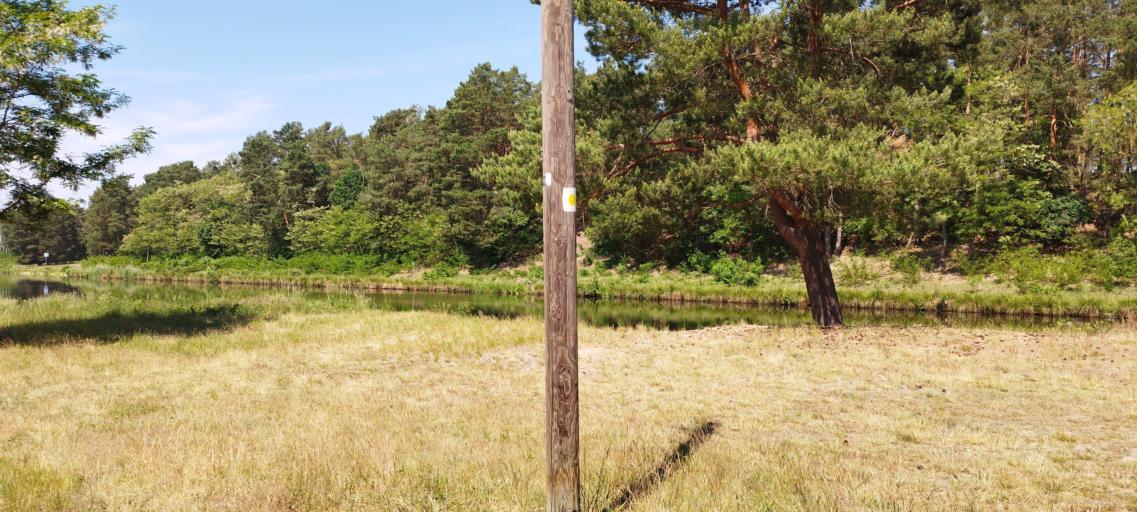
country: DE
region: Brandenburg
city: Rauen
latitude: 52.3642
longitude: 13.9579
